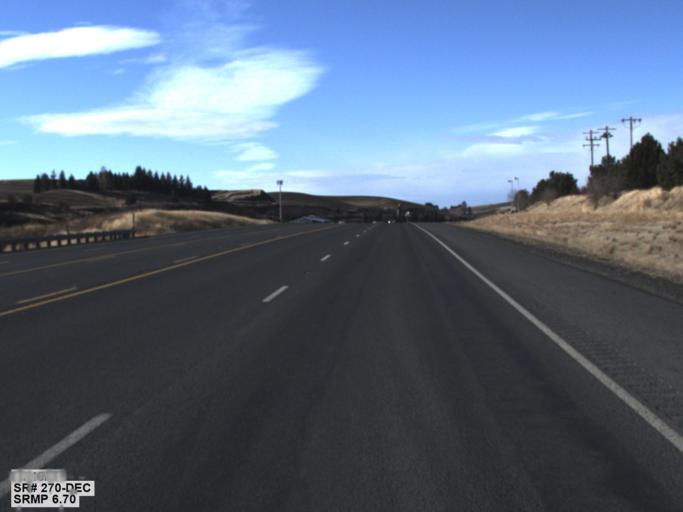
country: US
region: Washington
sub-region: Whitman County
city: Pullman
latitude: 46.7288
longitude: -117.1009
